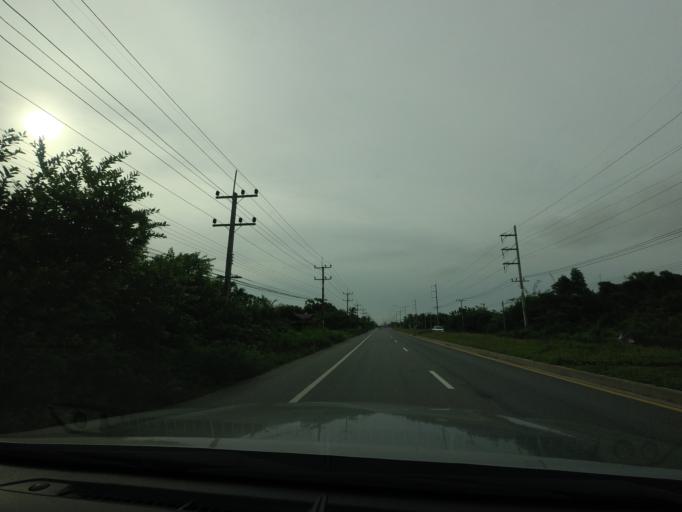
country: TH
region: Songkhla
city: Ranot
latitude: 7.7373
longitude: 100.3650
